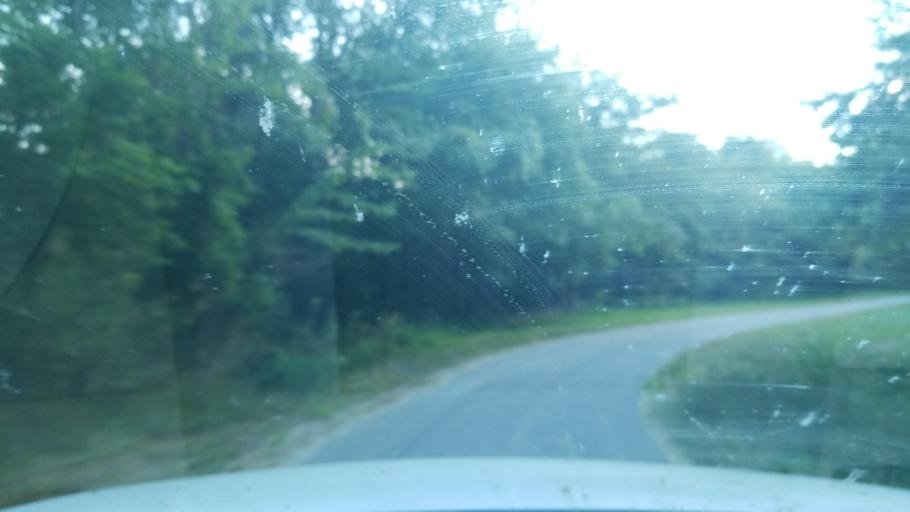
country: US
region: Illinois
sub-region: Saline County
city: Carrier Mills
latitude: 37.7893
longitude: -88.7056
